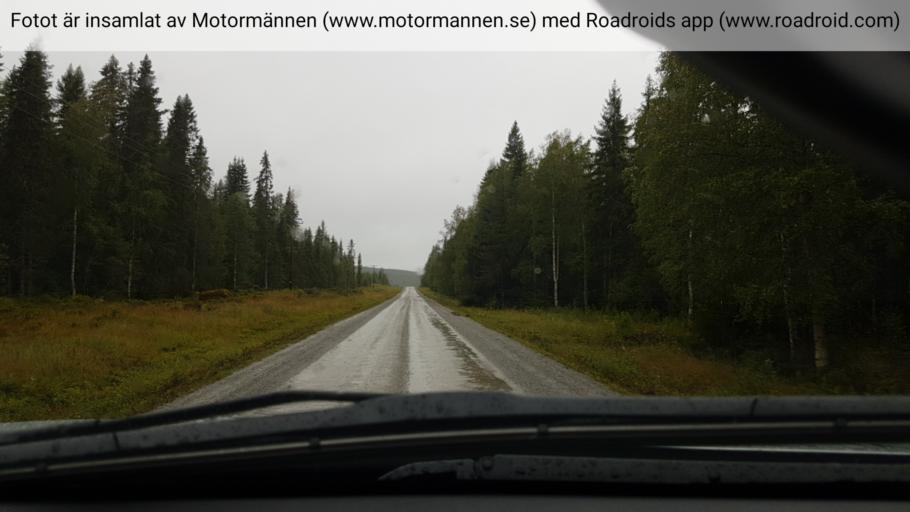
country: SE
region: Vaesterbotten
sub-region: Asele Kommun
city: Insjon
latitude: 64.0869
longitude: 17.8466
